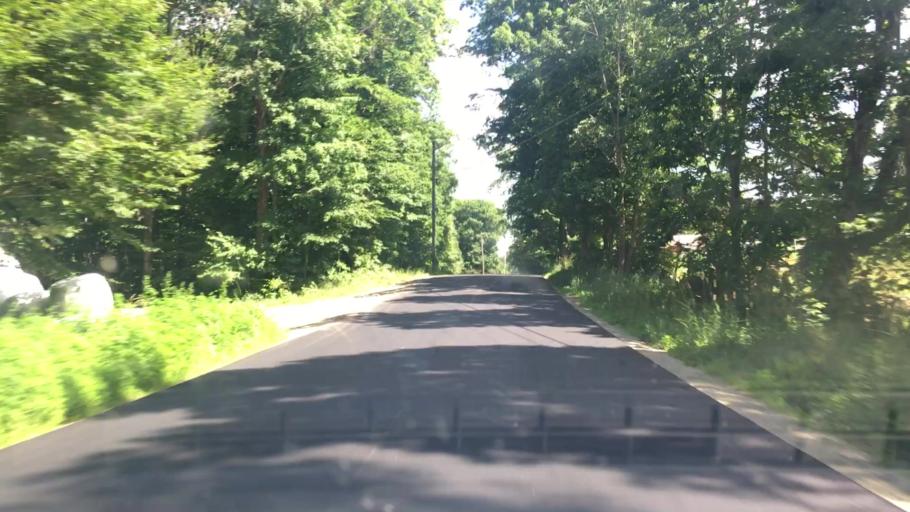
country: US
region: Maine
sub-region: Franklin County
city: Chesterville
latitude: 44.5691
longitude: -70.1480
